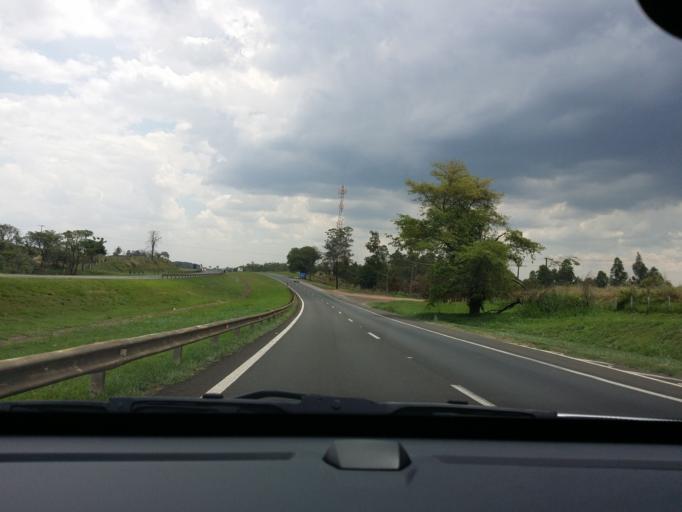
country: BR
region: Sao Paulo
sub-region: Rio Claro
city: Rio Claro
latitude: -22.3628
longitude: -47.6322
